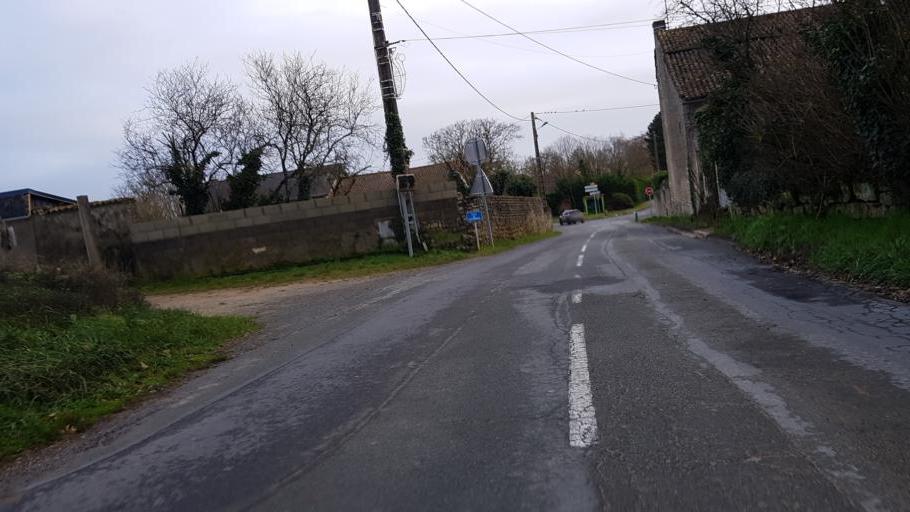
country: FR
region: Poitou-Charentes
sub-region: Departement de la Vienne
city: Avanton
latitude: 46.6597
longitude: 0.3339
